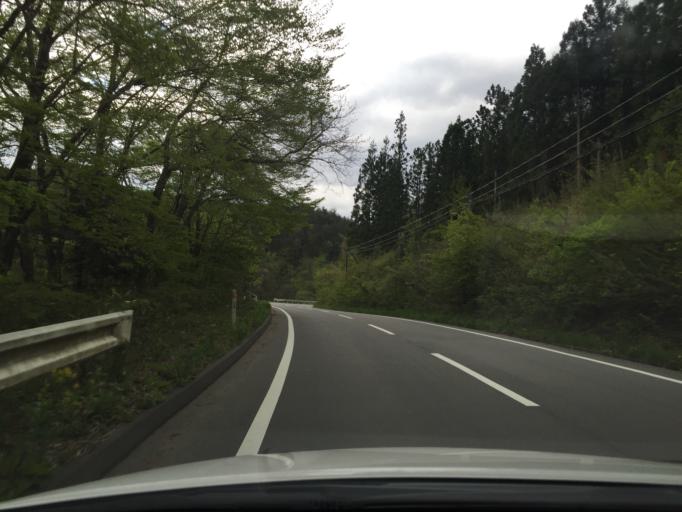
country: JP
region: Fukushima
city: Yanagawamachi-saiwaicho
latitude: 37.7302
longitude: 140.7338
